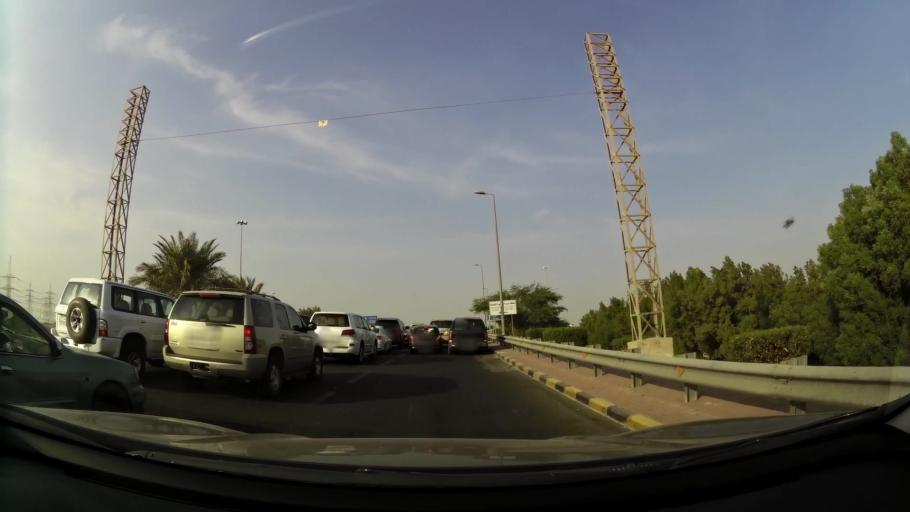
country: KW
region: Mubarak al Kabir
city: Mubarak al Kabir
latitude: 29.2049
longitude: 48.0607
